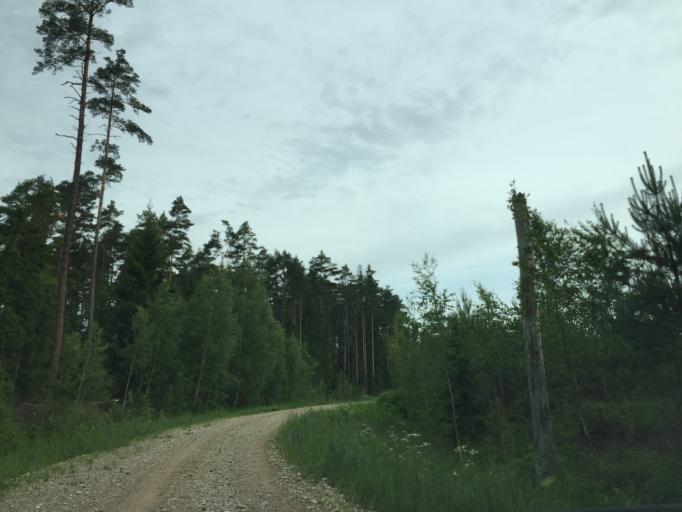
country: LV
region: Tukuma Rajons
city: Tukums
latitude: 57.0309
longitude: 23.1598
